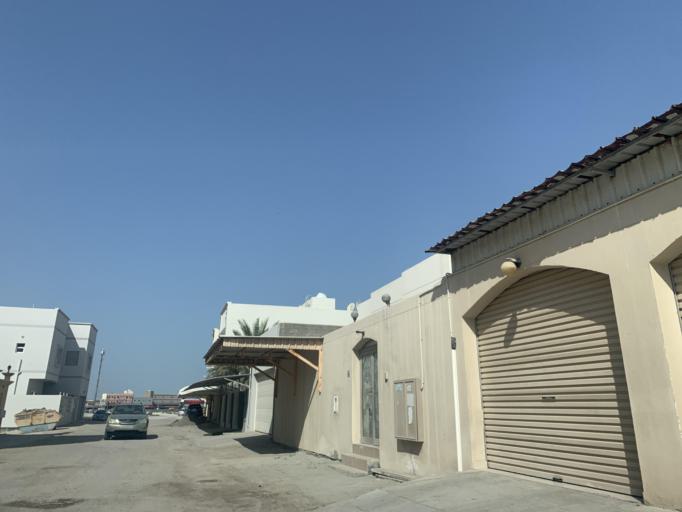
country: BH
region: Central Governorate
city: Madinat Hamad
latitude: 26.1362
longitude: 50.4901
